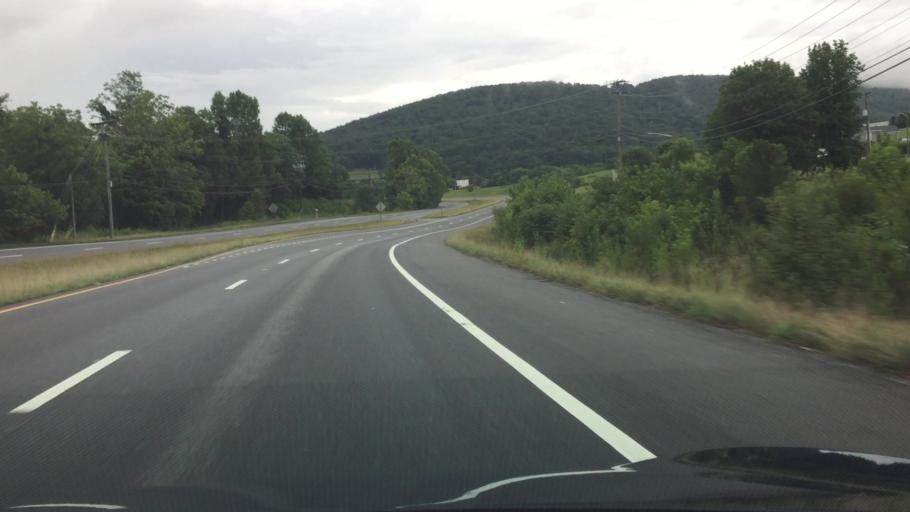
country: US
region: Virginia
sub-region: Botetourt County
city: Laymantown
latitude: 37.3366
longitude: -79.8754
